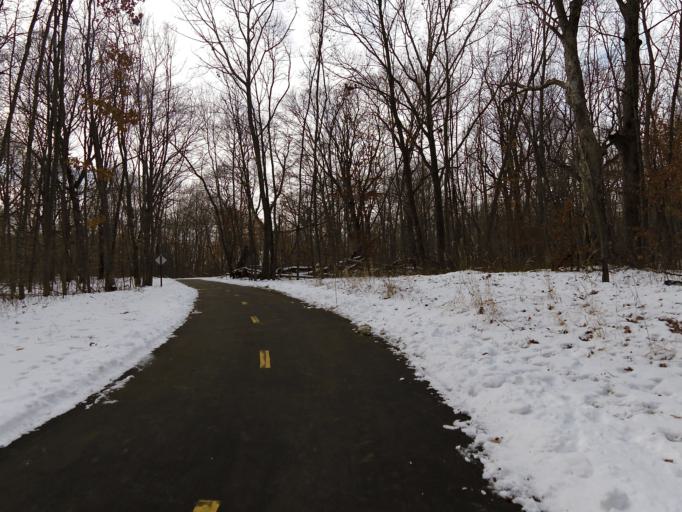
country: US
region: Minnesota
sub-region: Scott County
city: Prior Lake
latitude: 44.7139
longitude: -93.4726
